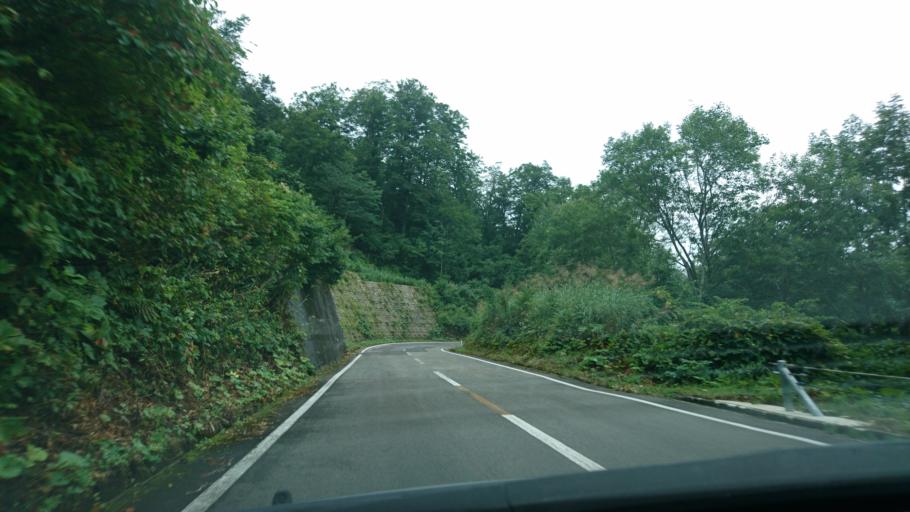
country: JP
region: Akita
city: Yuzawa
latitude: 38.9851
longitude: 140.7299
